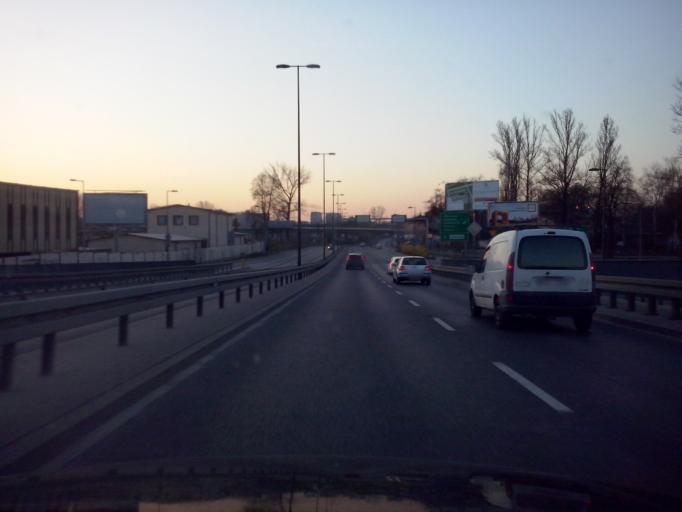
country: PL
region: Lesser Poland Voivodeship
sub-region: Krakow
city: Krakow
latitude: 50.0717
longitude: 19.9485
